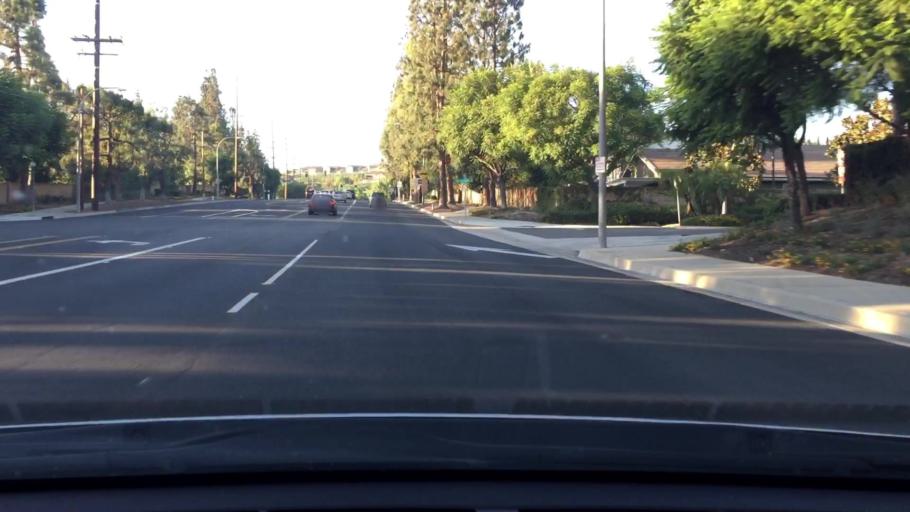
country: US
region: California
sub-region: Orange County
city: Brea
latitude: 33.9211
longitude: -117.8638
